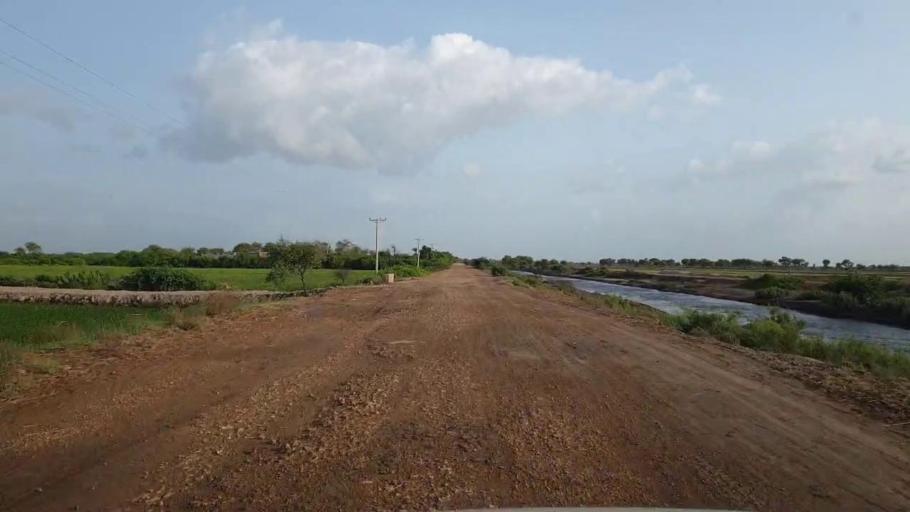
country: PK
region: Sindh
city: Kario
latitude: 24.8137
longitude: 68.6468
